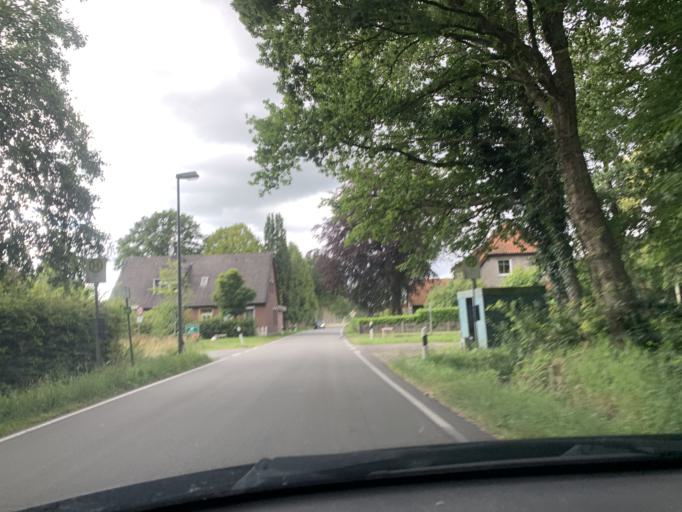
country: DE
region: Lower Saxony
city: Westerstede
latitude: 53.2210
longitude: 7.9079
